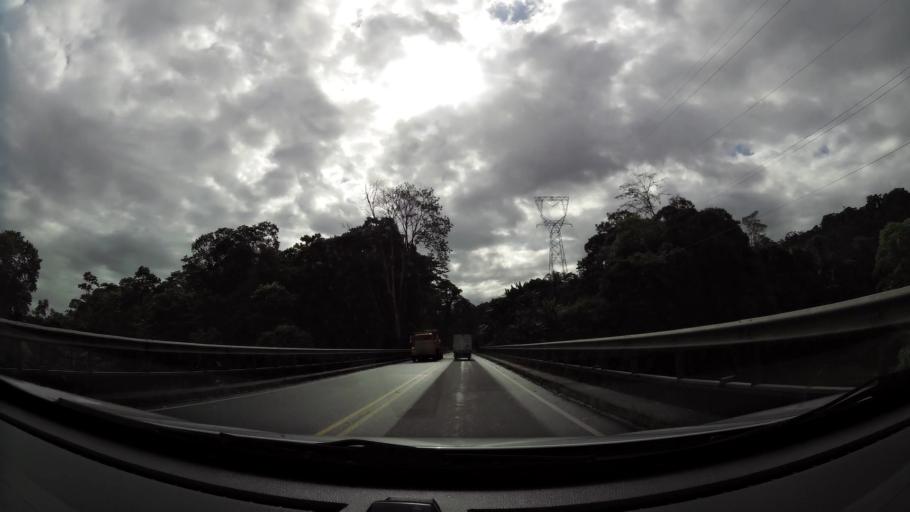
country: CR
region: Limon
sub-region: Canton de Siquirres
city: Siquirres
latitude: 10.1056
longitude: -83.5305
